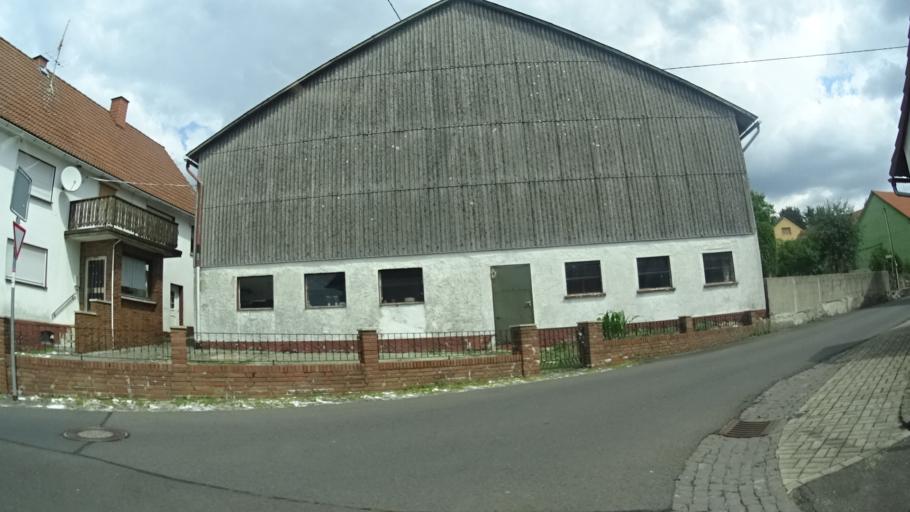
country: DE
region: Hesse
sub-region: Regierungsbezirk Giessen
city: Grebenhain
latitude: 50.4469
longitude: 9.2796
